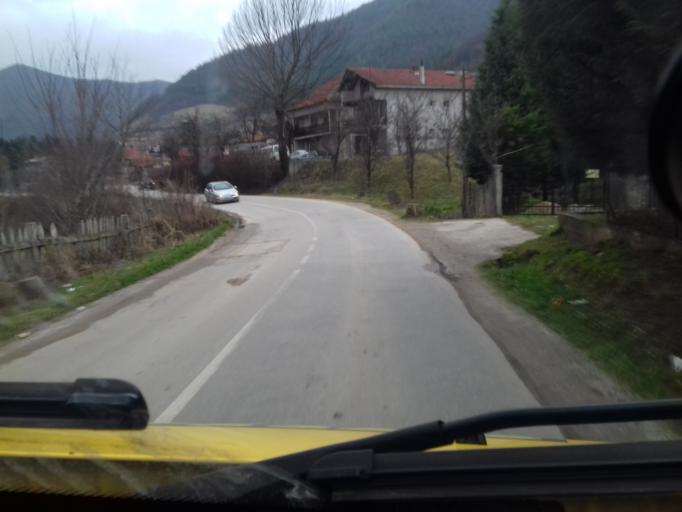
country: BA
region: Federation of Bosnia and Herzegovina
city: Zenica
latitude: 44.1612
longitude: 17.9626
